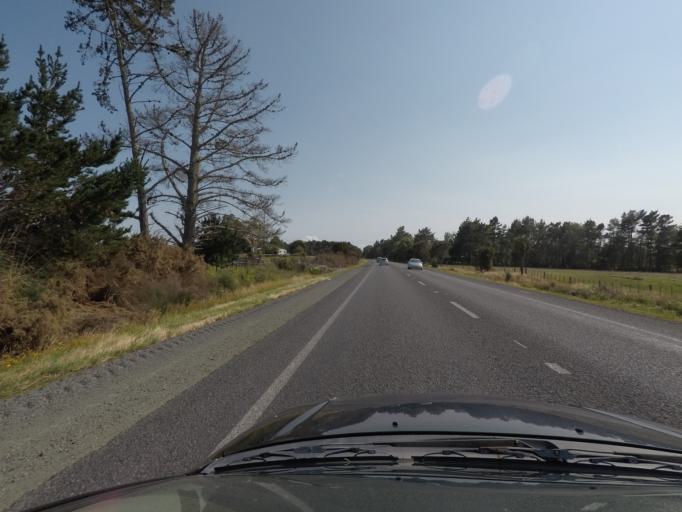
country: NZ
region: Northland
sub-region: Whangarei
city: Ruakaka
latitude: -35.9607
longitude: 174.4486
